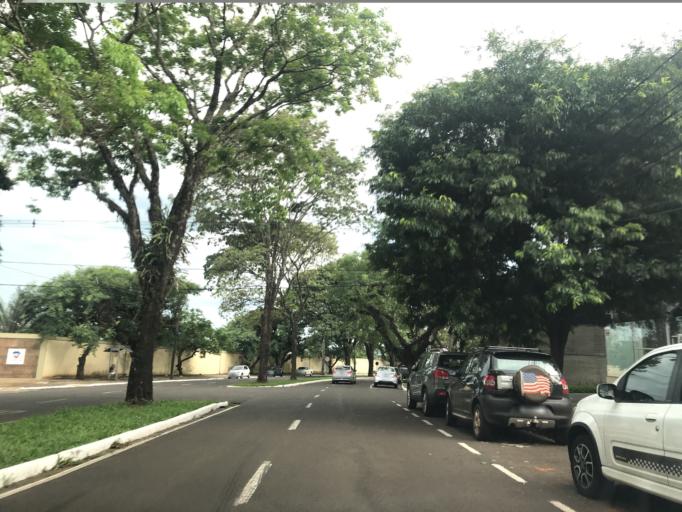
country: BR
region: Parana
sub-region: Maringa
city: Maringa
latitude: -23.4341
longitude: -51.9483
